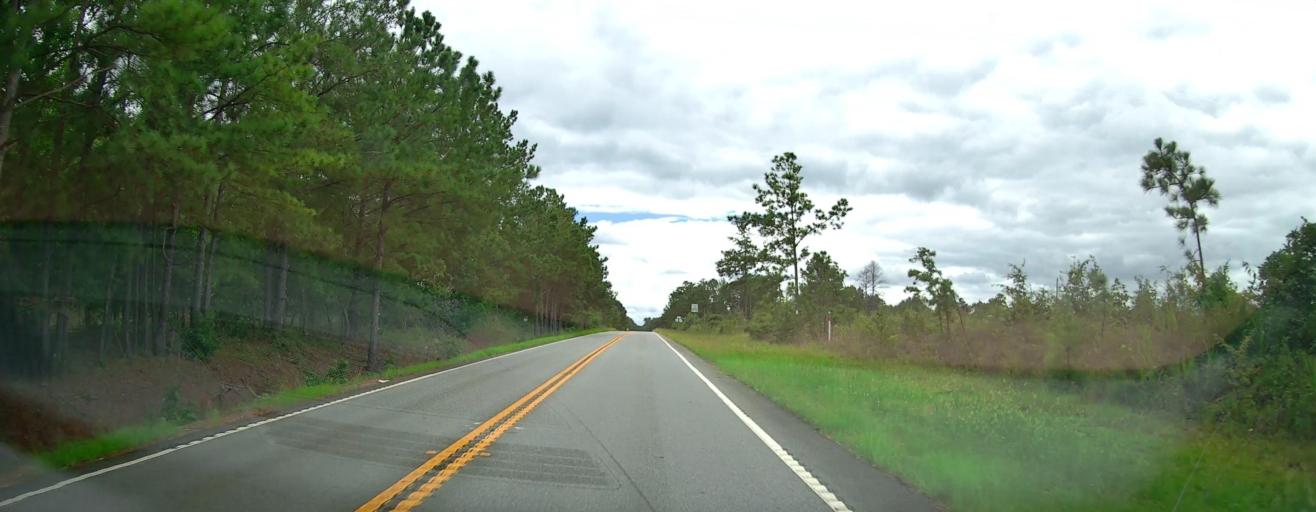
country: US
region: Georgia
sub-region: Twiggs County
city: Jeffersonville
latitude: 32.6693
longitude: -83.3266
